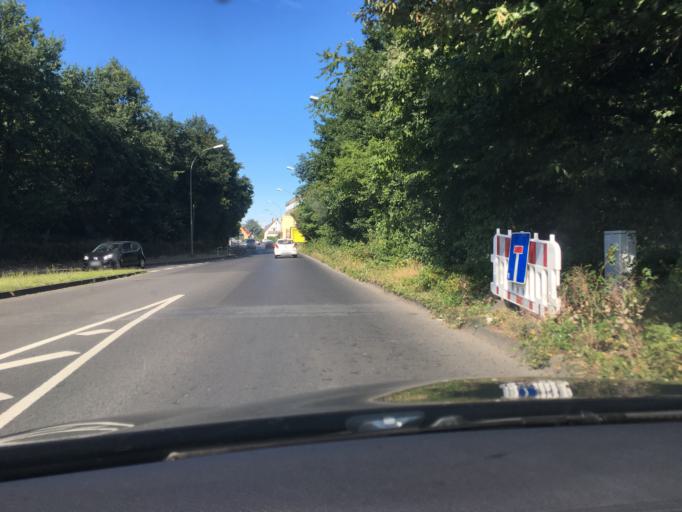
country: DE
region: Hesse
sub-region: Regierungsbezirk Darmstadt
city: Offenbach
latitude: 50.1403
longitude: 8.7544
